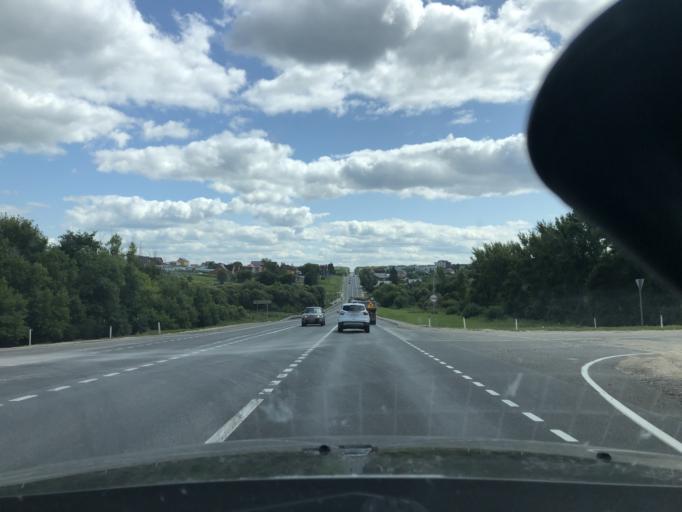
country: RU
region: Tula
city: Gorelki
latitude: 54.3069
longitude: 37.5700
